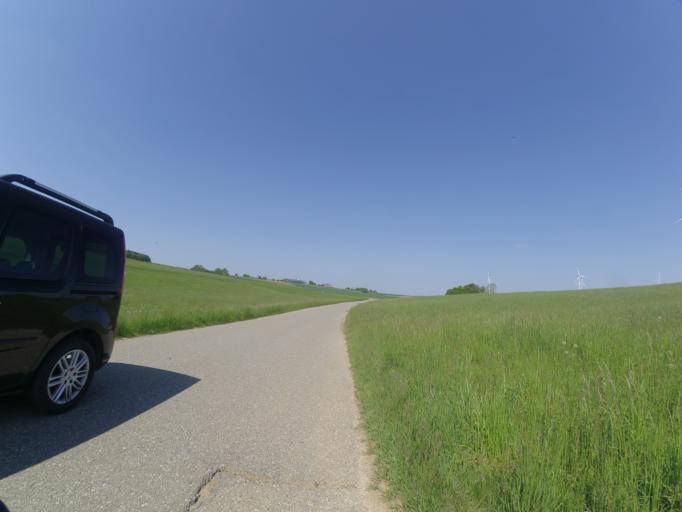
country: DE
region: Baden-Wuerttemberg
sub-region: Tuebingen Region
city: Dornstadt
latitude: 48.4613
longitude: 9.8760
